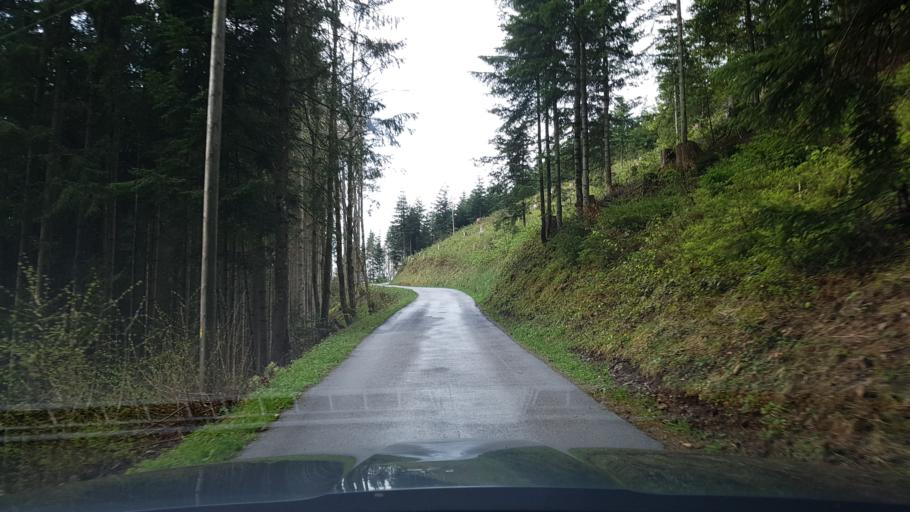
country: AT
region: Salzburg
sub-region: Politischer Bezirk Sankt Johann im Pongau
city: Werfen
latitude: 47.4646
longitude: 13.1796
